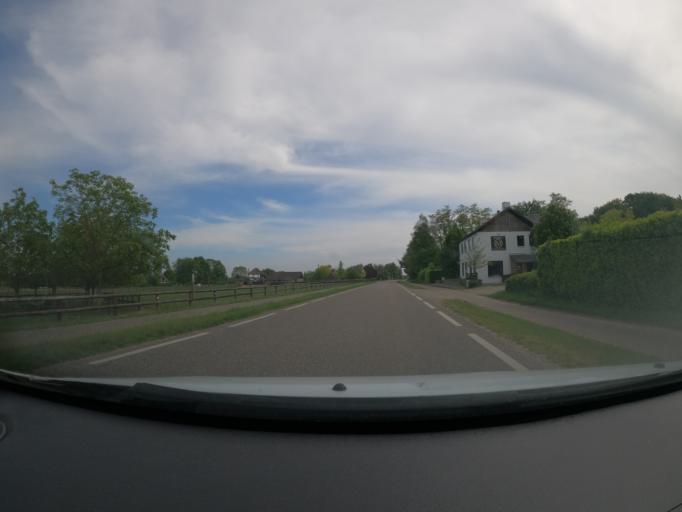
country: NL
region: Gelderland
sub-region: Gemeente Montferland
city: s-Heerenberg
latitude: 51.9204
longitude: 6.2507
